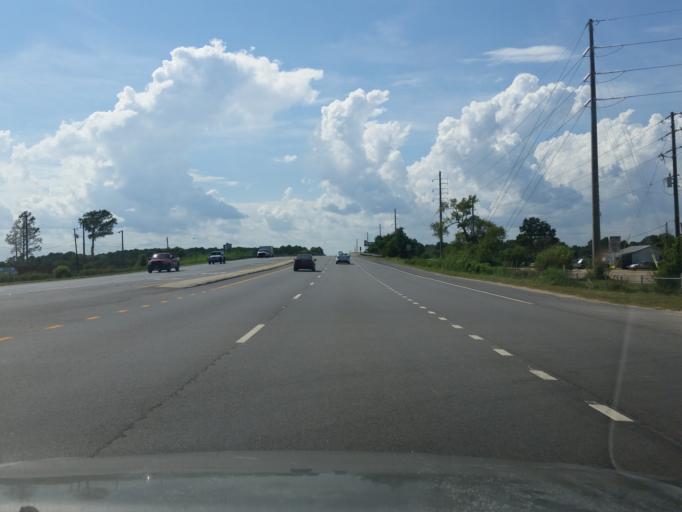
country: US
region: Alabama
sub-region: Baldwin County
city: Spanish Fort
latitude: 30.6675
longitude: -87.9215
